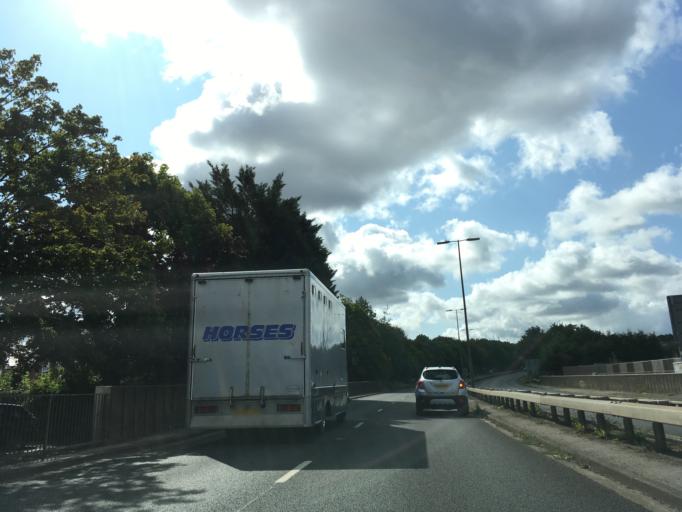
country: GB
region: England
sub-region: West Berkshire
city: Newbury
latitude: 51.3953
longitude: -1.3198
